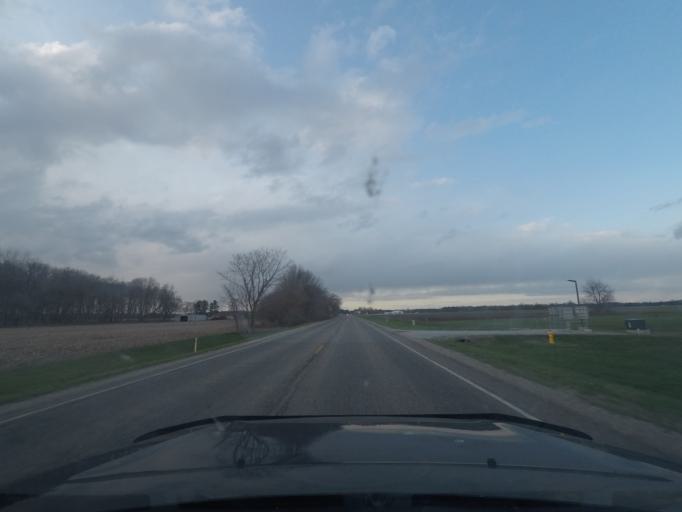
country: US
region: Indiana
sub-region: LaPorte County
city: LaPorte
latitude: 41.5725
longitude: -86.7394
